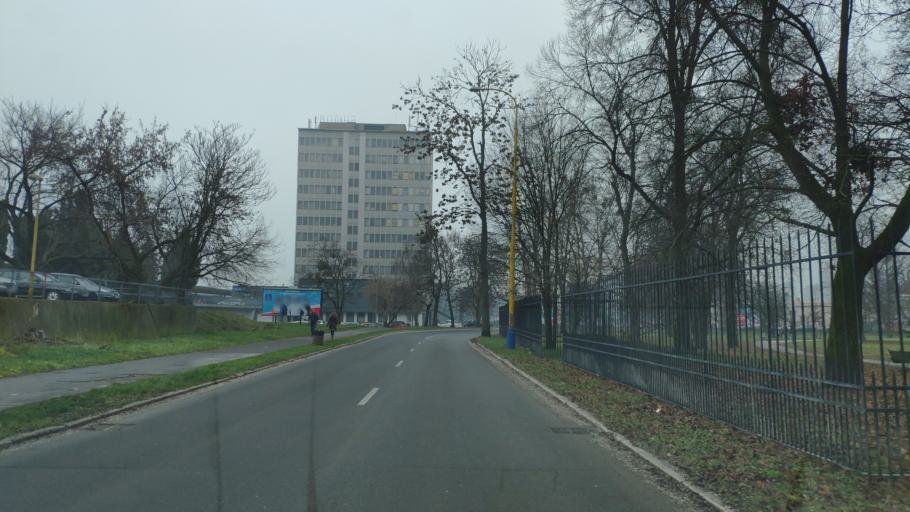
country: SK
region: Kosicky
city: Kosice
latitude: 48.7246
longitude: 21.2665
